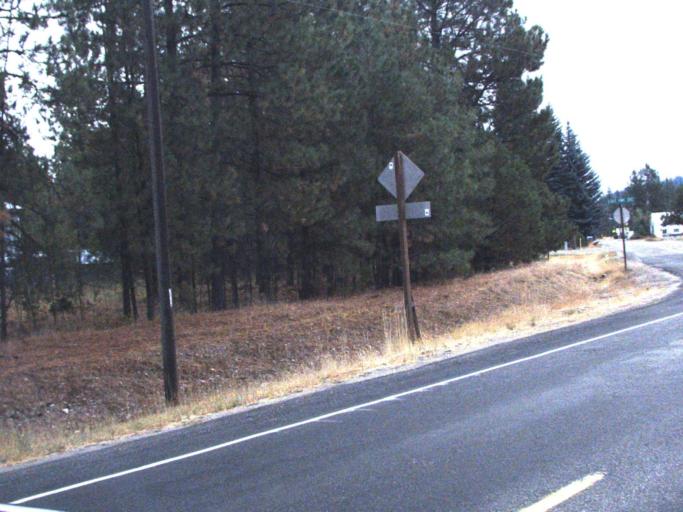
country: US
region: Washington
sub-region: Spokane County
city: Deer Park
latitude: 48.0628
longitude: -117.6369
